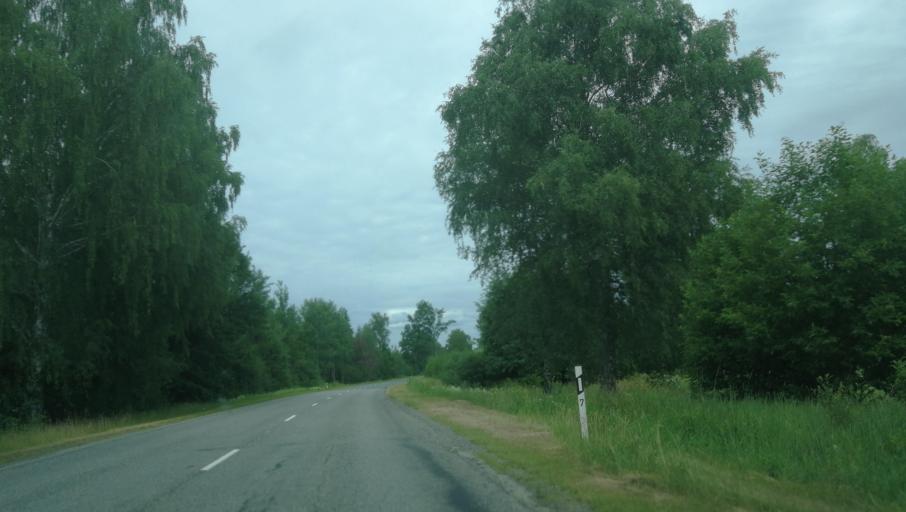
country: LV
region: Valmieras Rajons
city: Valmiera
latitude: 57.6525
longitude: 25.4319
